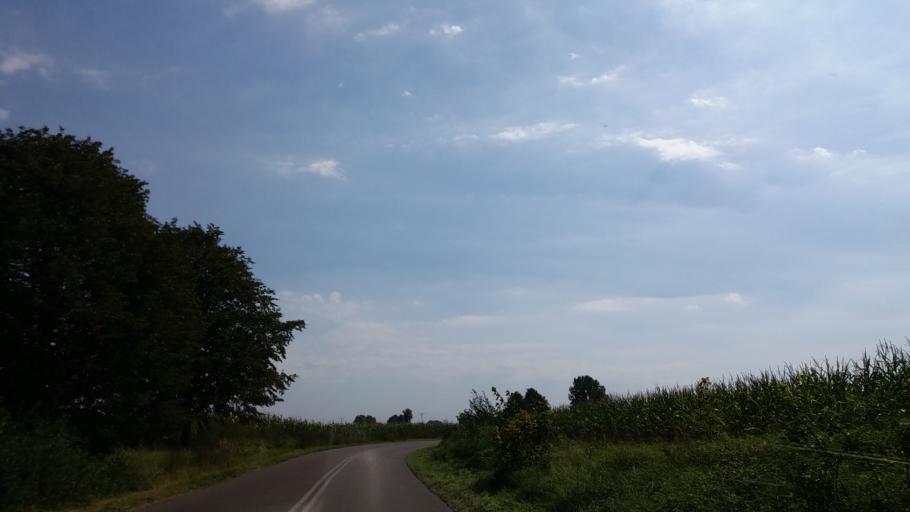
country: PL
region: West Pomeranian Voivodeship
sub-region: Powiat choszczenski
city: Krzecin
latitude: 53.1111
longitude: 15.4581
